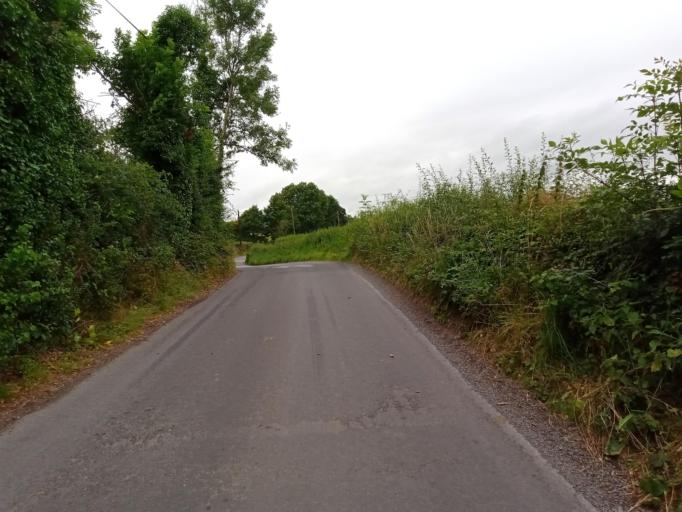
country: IE
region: Leinster
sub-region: Kilkenny
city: Ballyragget
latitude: 52.8091
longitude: -7.4324
